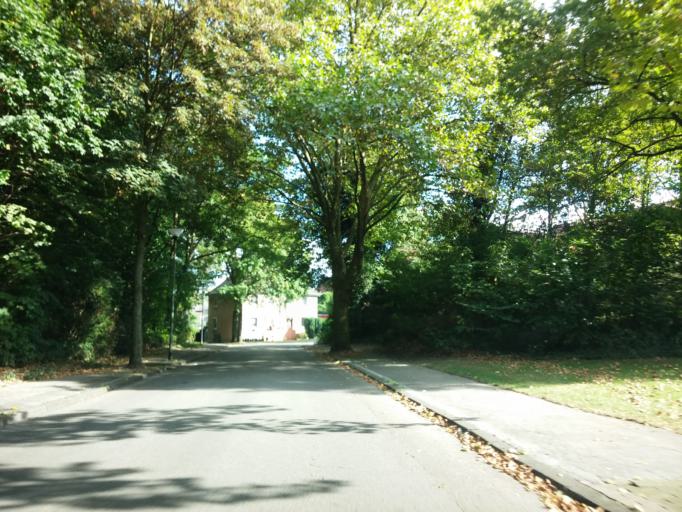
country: DE
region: North Rhine-Westphalia
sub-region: Regierungsbezirk Munster
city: Gladbeck
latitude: 51.5940
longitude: 7.0101
